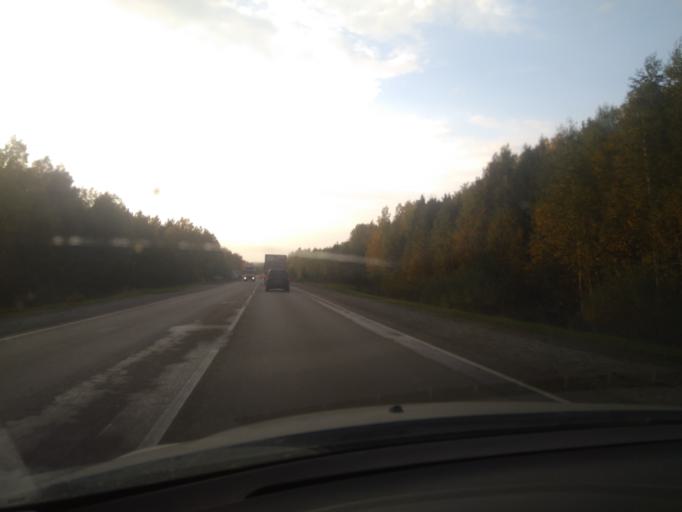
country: RU
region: Sverdlovsk
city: Verkhneye Dubrovo
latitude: 56.7262
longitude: 61.0391
